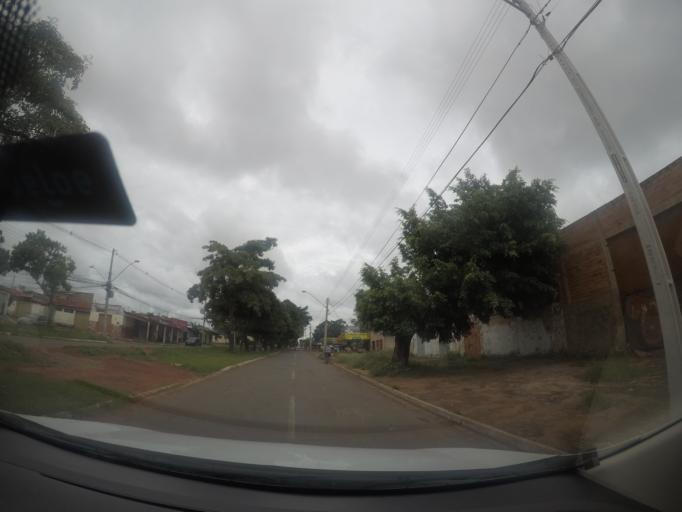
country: BR
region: Goias
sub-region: Trindade
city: Trindade
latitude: -16.6844
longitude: -49.3867
